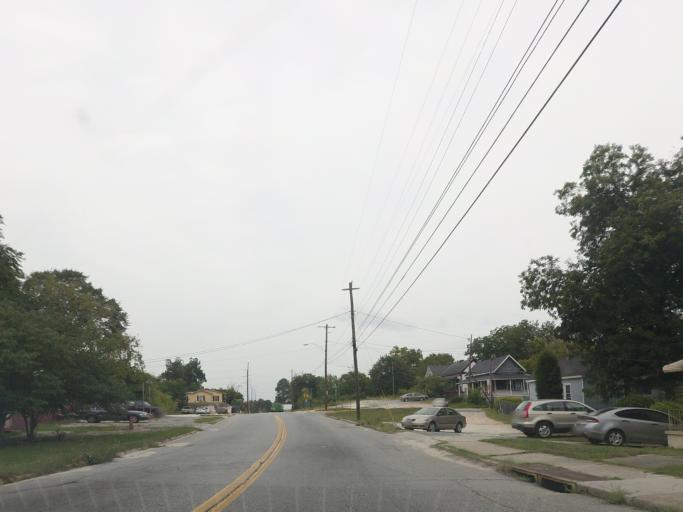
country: US
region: Georgia
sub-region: Bibb County
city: Macon
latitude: 32.8232
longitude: -83.6444
